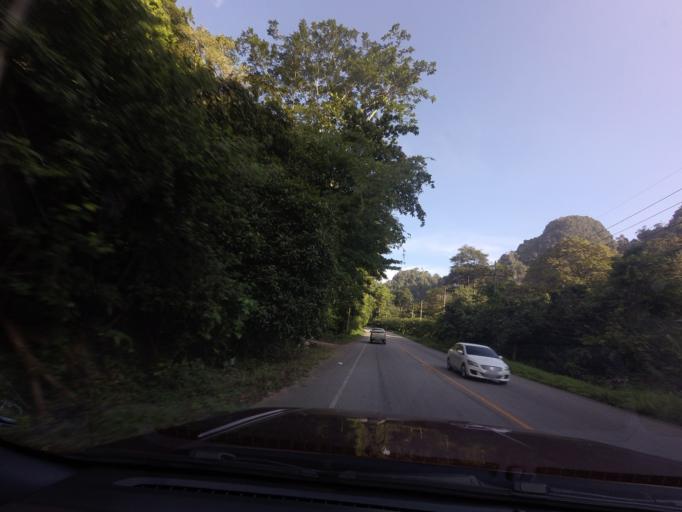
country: TH
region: Yala
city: Than To
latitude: 6.1816
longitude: 101.1740
